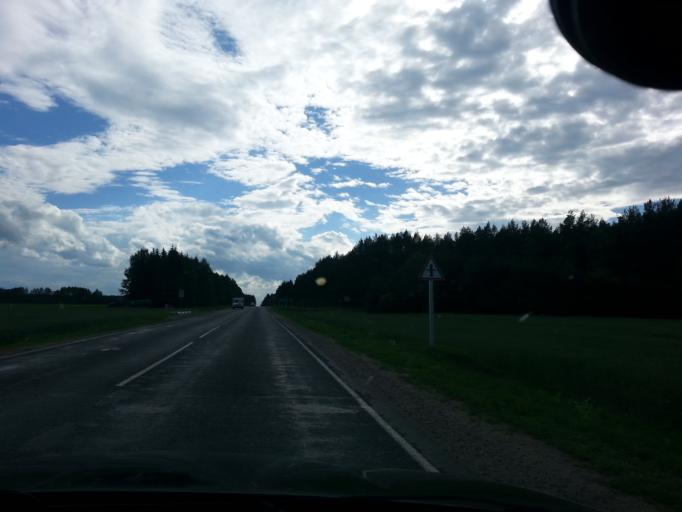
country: BY
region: Grodnenskaya
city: Astravyets
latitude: 54.7953
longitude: 26.1029
